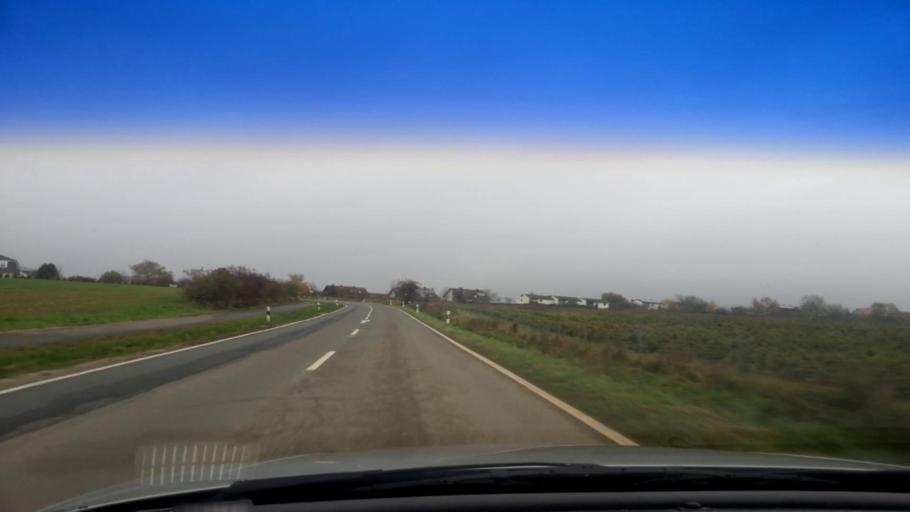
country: DE
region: Bavaria
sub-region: Upper Franconia
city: Litzendorf
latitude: 49.9055
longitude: 11.0122
